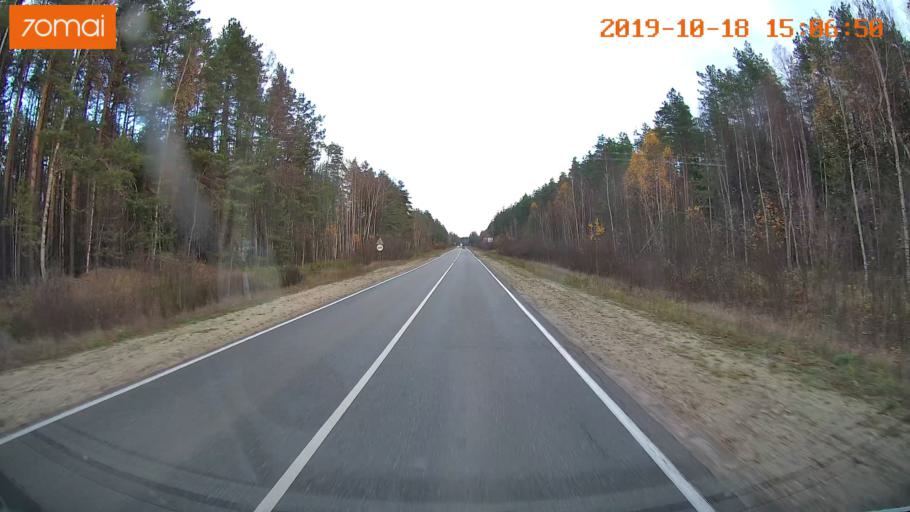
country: RU
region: Vladimir
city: Gus'-Khrustal'nyy
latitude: 55.5346
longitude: 40.5842
